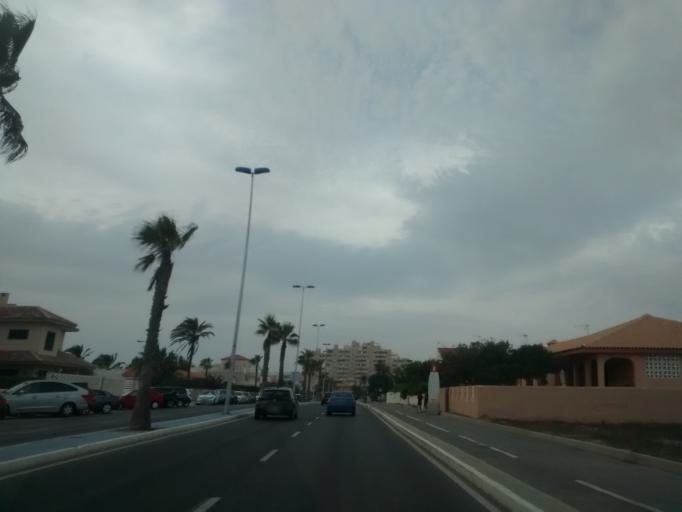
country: ES
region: Murcia
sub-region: Murcia
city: La Manga del Mar Menor
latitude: 37.7006
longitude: -0.7404
